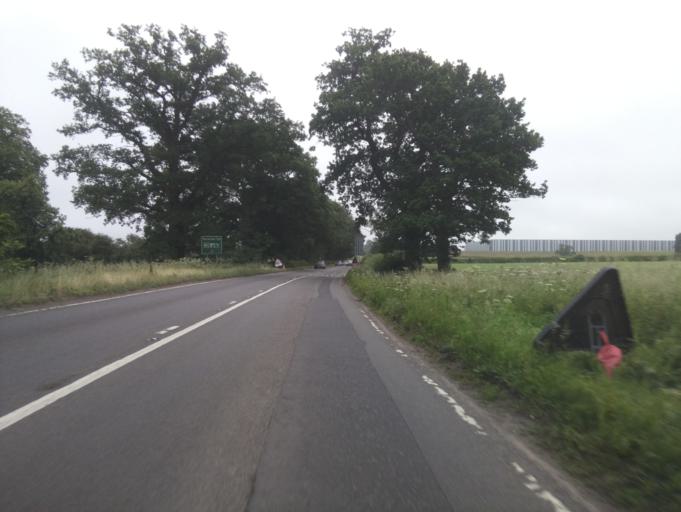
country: GB
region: England
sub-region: Derbyshire
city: Netherseal
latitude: 52.6977
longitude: -1.5546
